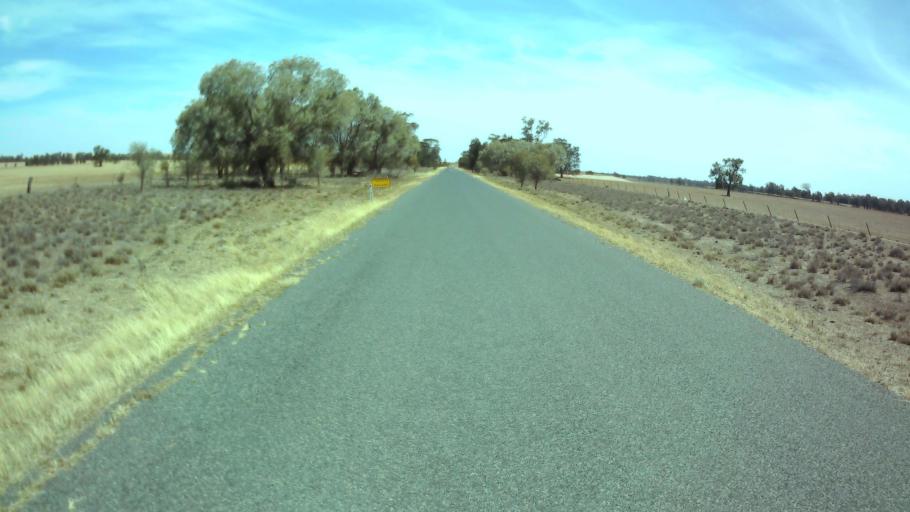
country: AU
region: New South Wales
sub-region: Weddin
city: Grenfell
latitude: -33.8791
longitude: 147.7432
